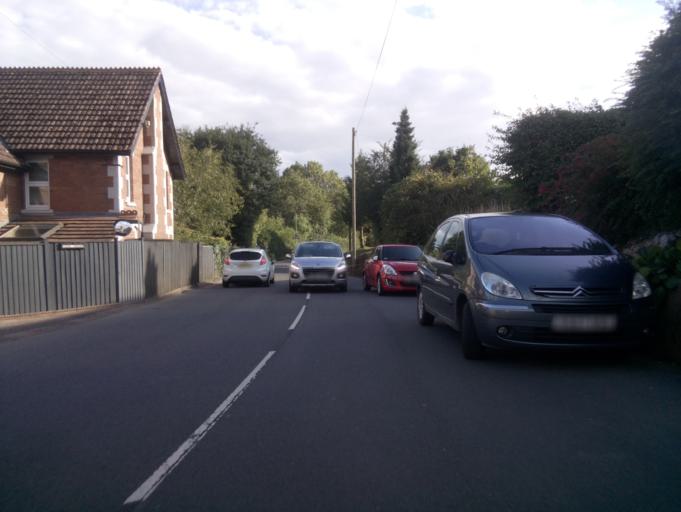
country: GB
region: England
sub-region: Devon
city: Sidmouth
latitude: 50.7131
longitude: -3.2239
